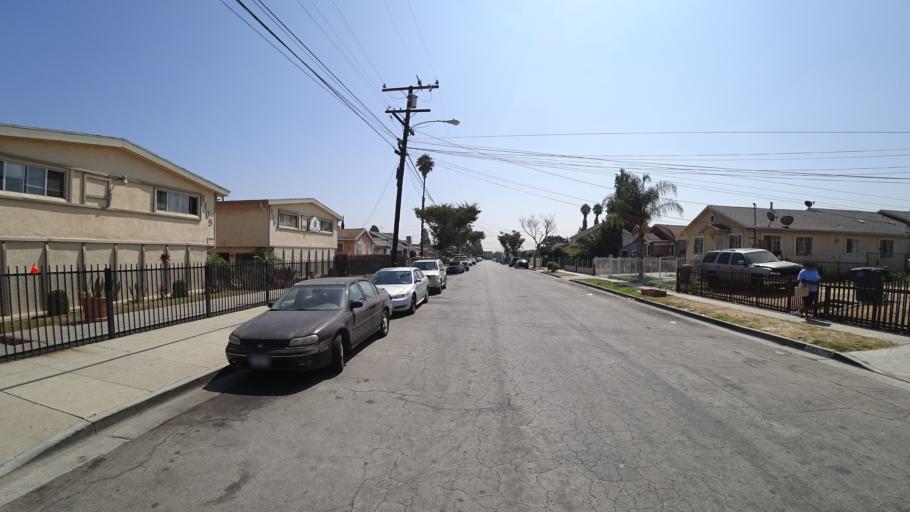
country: US
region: California
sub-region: Los Angeles County
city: Westmont
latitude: 33.9388
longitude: -118.2944
